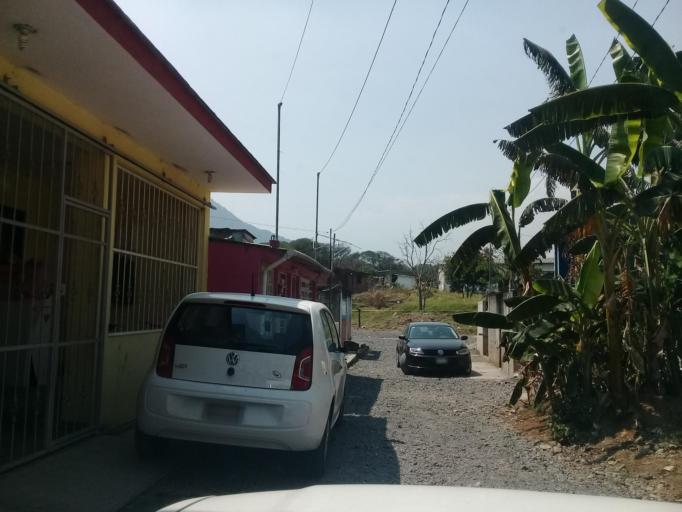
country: MX
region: Veracruz
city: Ixtac Zoquitlan
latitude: 18.8733
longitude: -97.0579
